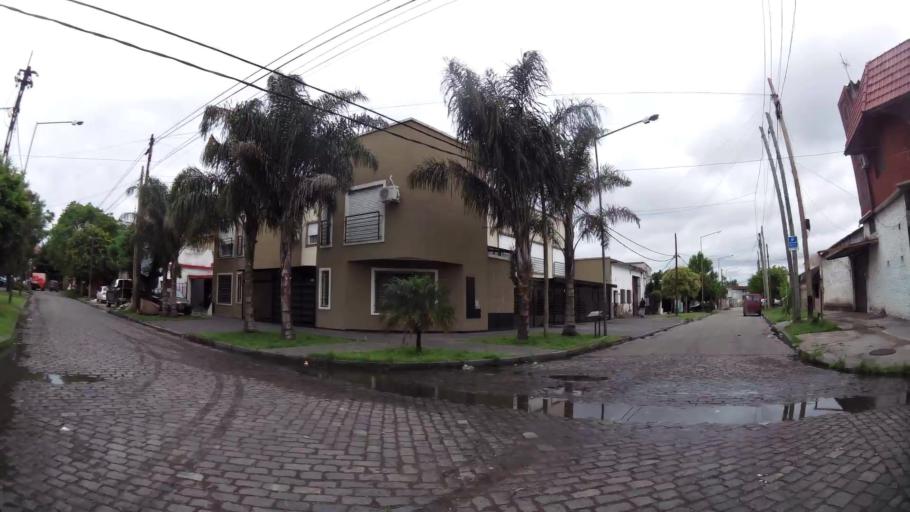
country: AR
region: Buenos Aires
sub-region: Partido de Lanus
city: Lanus
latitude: -34.7336
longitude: -58.3856
